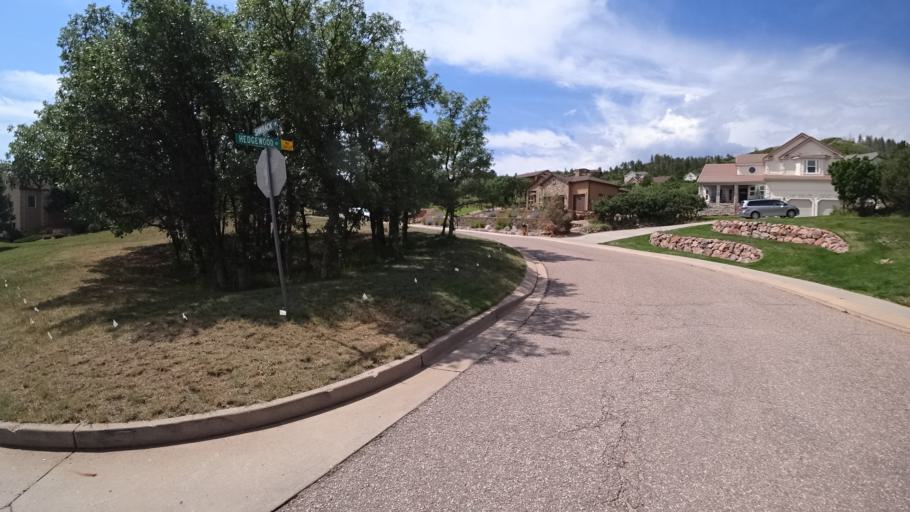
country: US
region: Colorado
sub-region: El Paso County
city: Air Force Academy
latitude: 38.9475
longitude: -104.8819
